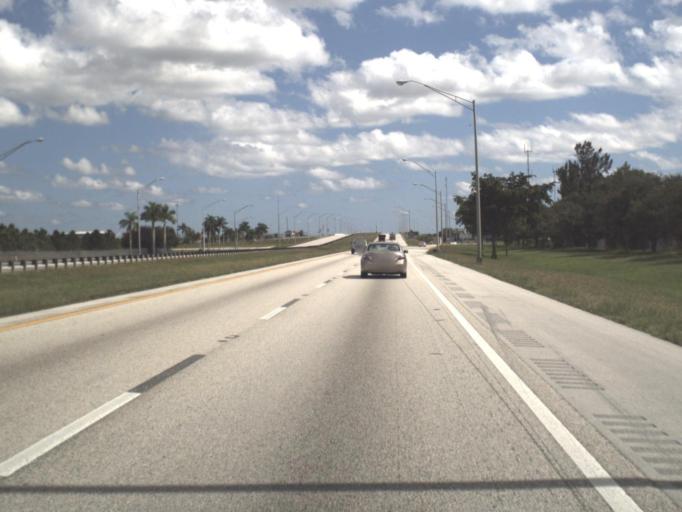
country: US
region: Florida
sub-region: Miami-Dade County
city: Lake Lucerne
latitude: 25.9720
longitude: -80.2542
